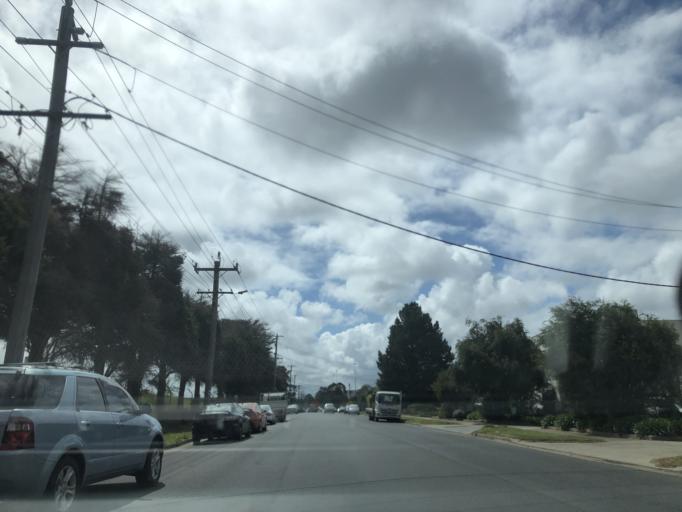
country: AU
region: Victoria
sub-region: Monash
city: Oakleigh South
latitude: -37.9321
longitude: 145.0939
